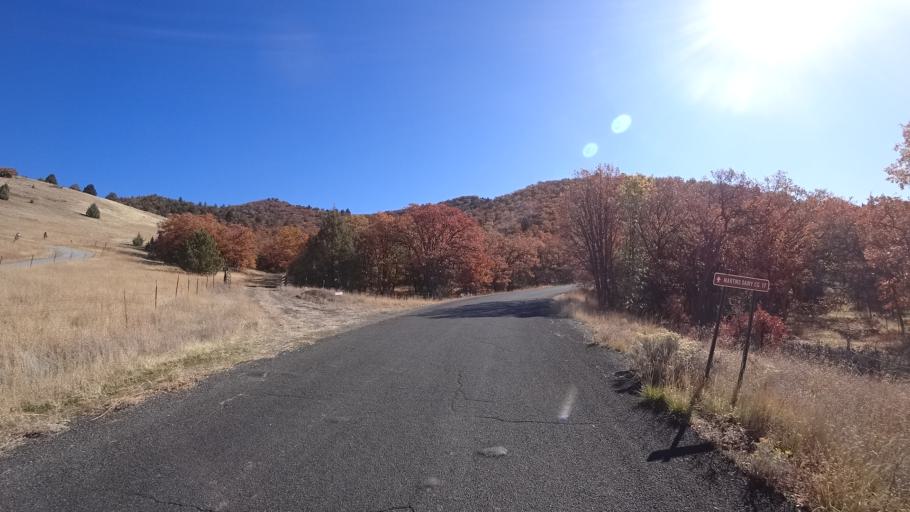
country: US
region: California
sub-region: Siskiyou County
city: Montague
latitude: 41.8304
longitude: -122.3426
